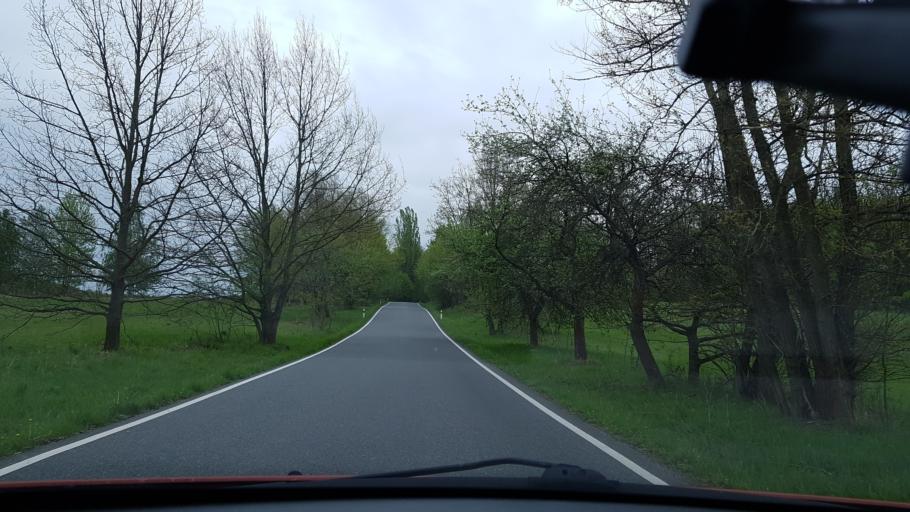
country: CZ
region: Olomoucky
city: Vidnava
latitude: 50.3646
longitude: 17.1996
